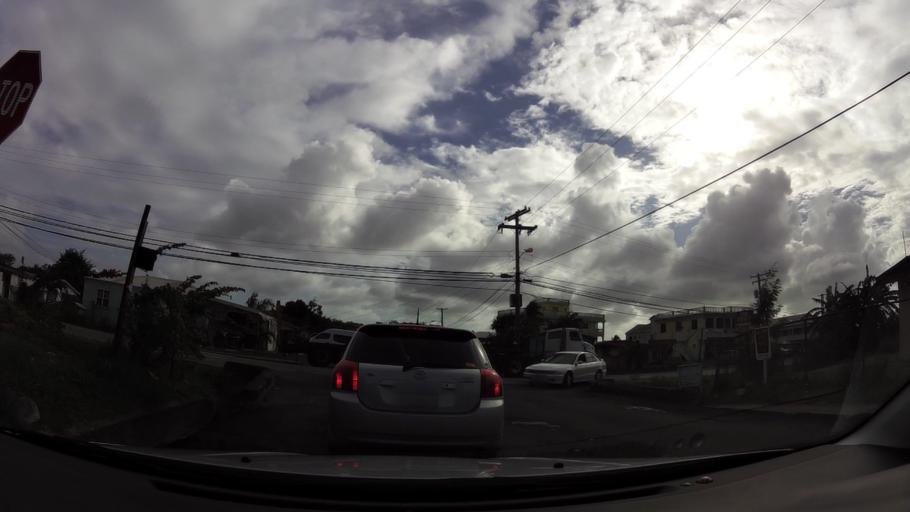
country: AG
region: Saint John
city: Saint John's
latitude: 17.1253
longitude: -61.8229
